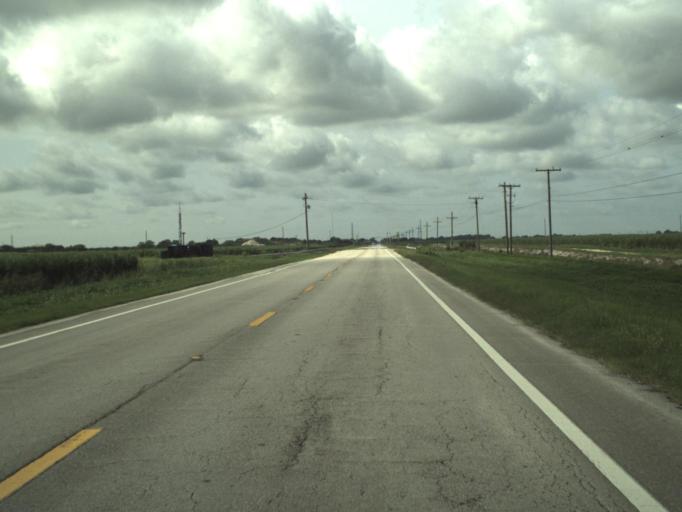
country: US
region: Florida
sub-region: Palm Beach County
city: Belle Glade
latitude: 26.7348
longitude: -80.6841
